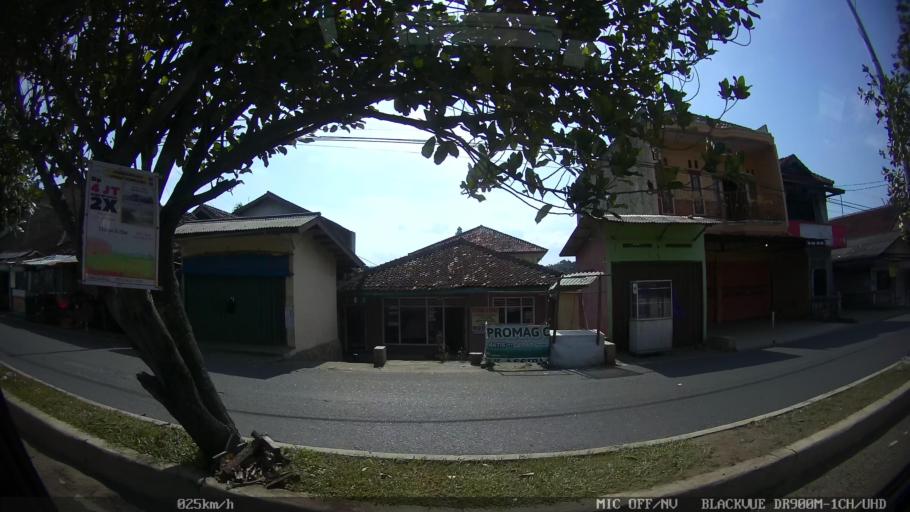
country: ID
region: Lampung
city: Kedaton
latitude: -5.3664
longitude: 105.2348
